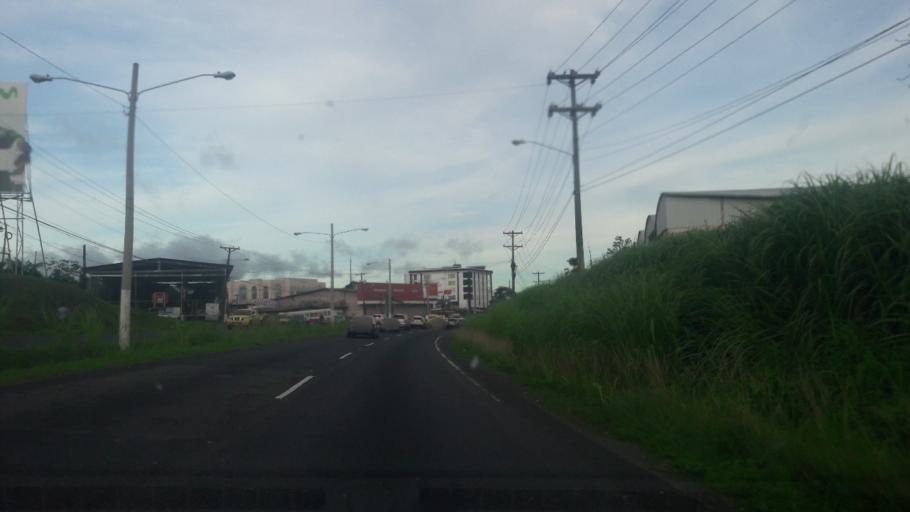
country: PA
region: Colon
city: Arco Iris
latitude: 9.3421
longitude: -79.8690
